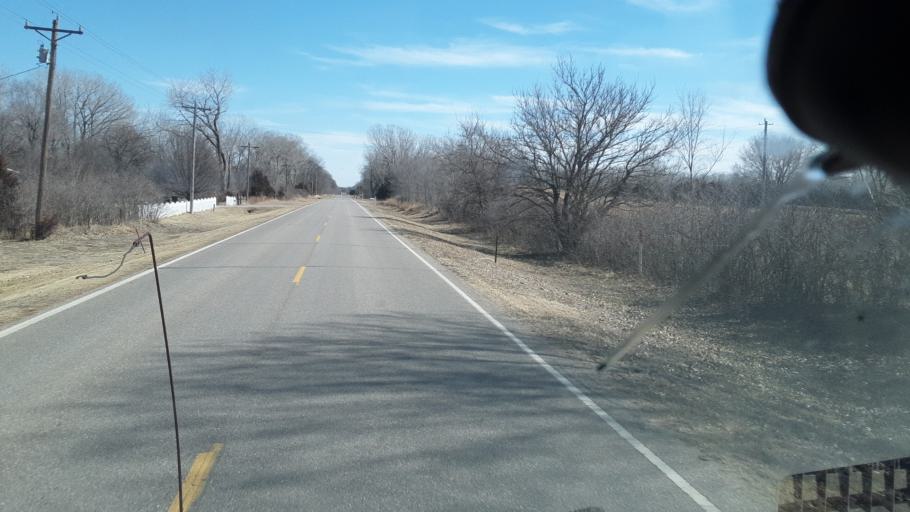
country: US
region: Kansas
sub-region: Reno County
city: Hutchinson
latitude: 38.1593
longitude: -97.8802
